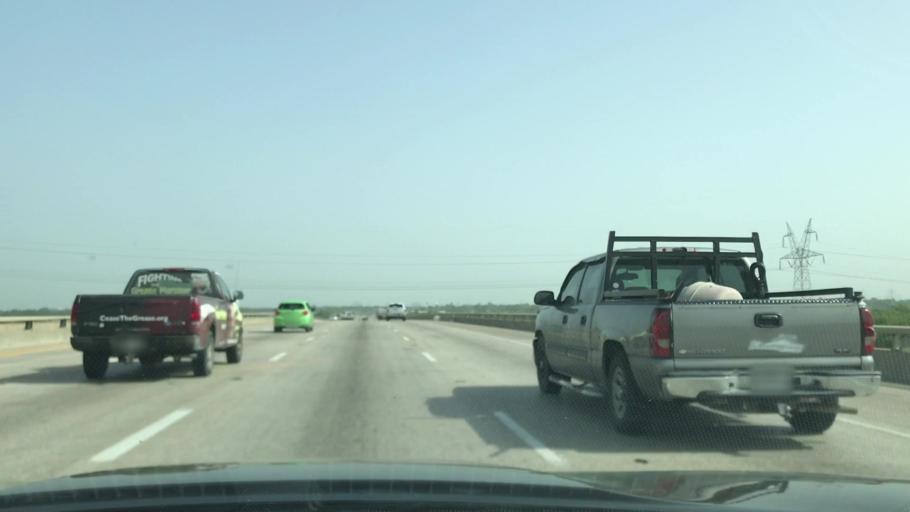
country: US
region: Texas
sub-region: Dallas County
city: Irving
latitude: 32.7852
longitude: -96.9184
